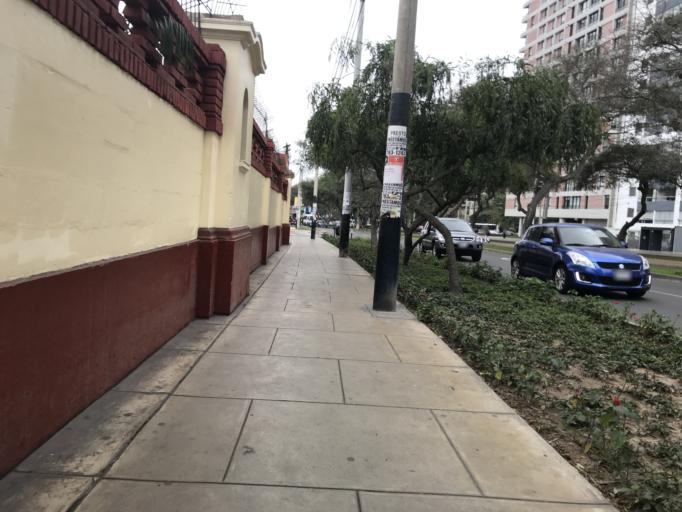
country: PE
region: Lima
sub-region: Lima
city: San Isidro
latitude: -12.0860
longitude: -77.0493
